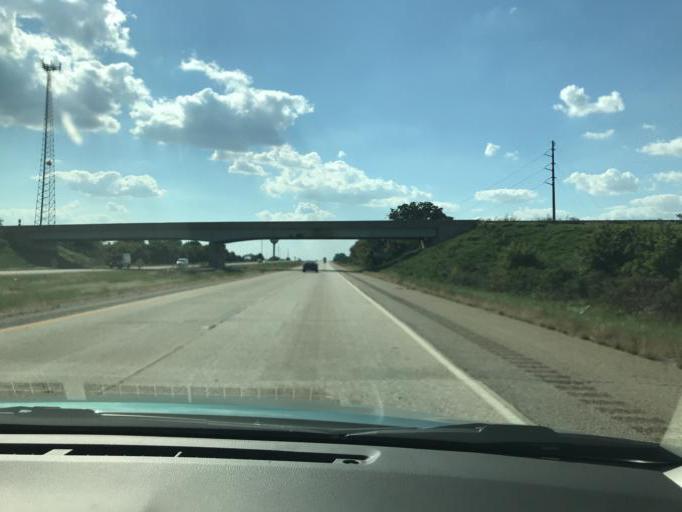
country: US
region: Wisconsin
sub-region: Walworth County
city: Darien
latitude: 42.6142
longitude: -88.7060
